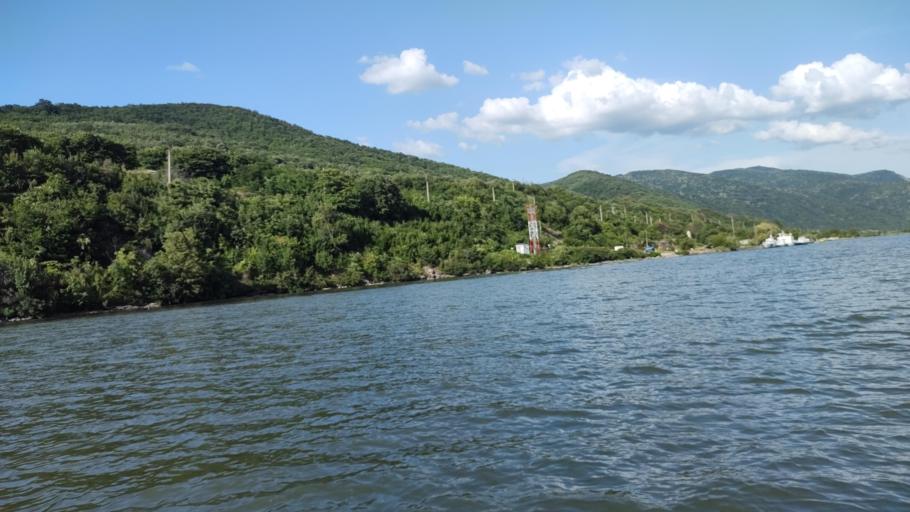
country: RO
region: Caras-Severin
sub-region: Comuna Berzasca
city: Berzasca
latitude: 44.6368
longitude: 21.9606
